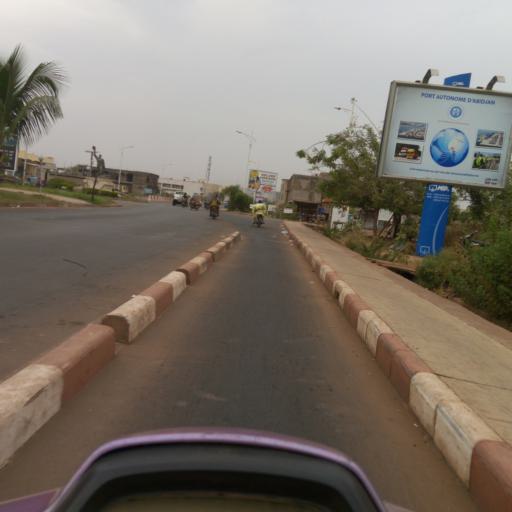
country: ML
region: Bamako
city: Bamako
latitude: 12.6557
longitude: -7.9317
